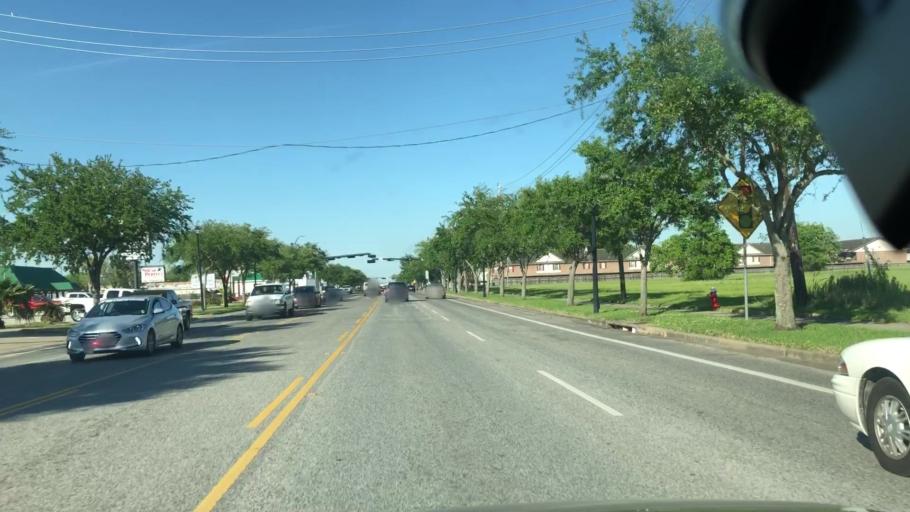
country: US
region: Texas
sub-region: Harris County
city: Webster
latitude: 29.5323
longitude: -95.1254
